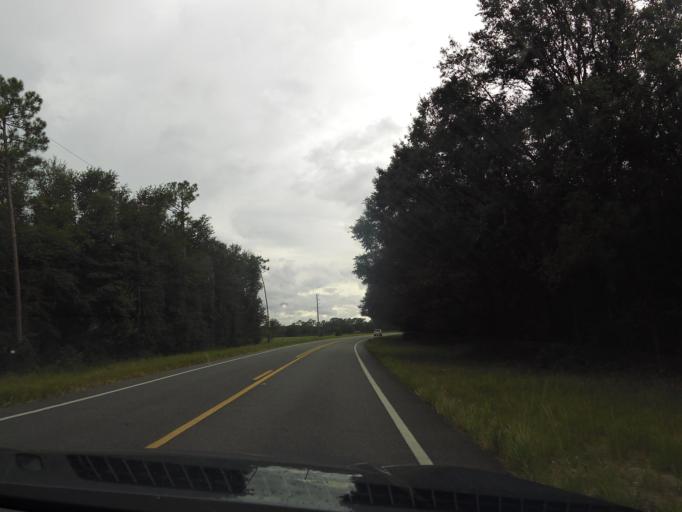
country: US
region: Florida
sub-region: Baker County
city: Macclenny
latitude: 30.3860
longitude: -82.1749
